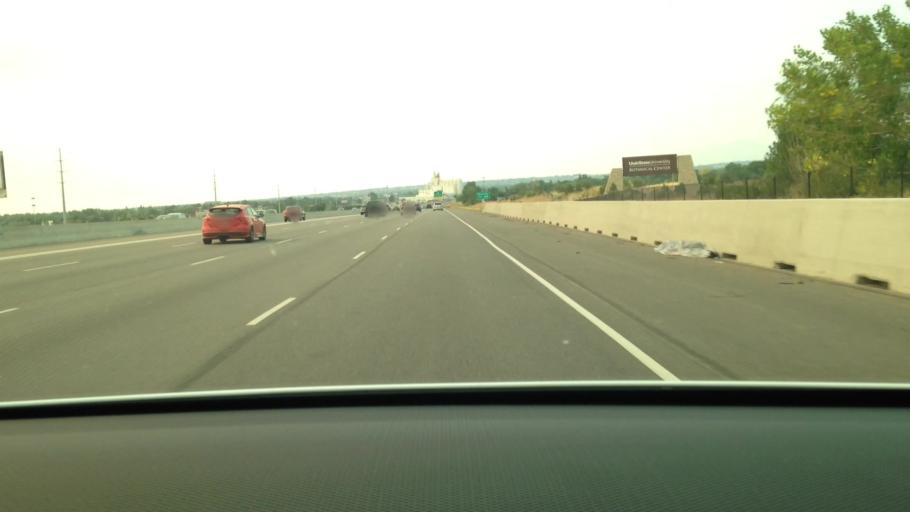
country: US
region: Utah
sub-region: Davis County
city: Kaysville
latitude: 41.0203
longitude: -111.9425
